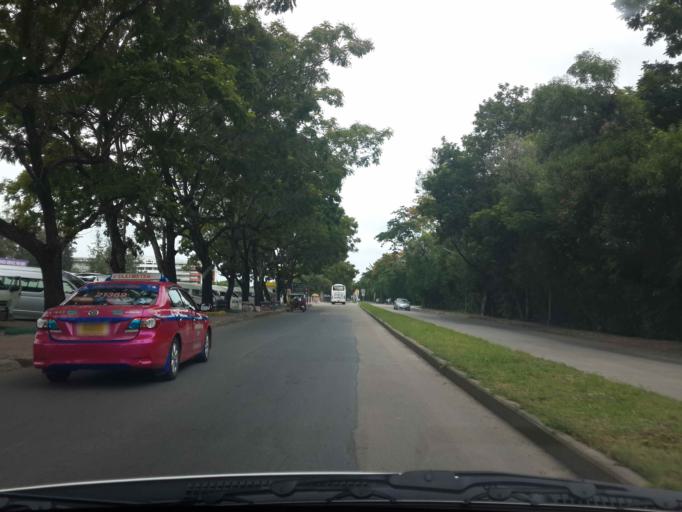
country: TH
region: Bangkok
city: Khlong Sam Wa
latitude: 13.8676
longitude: 100.7069
